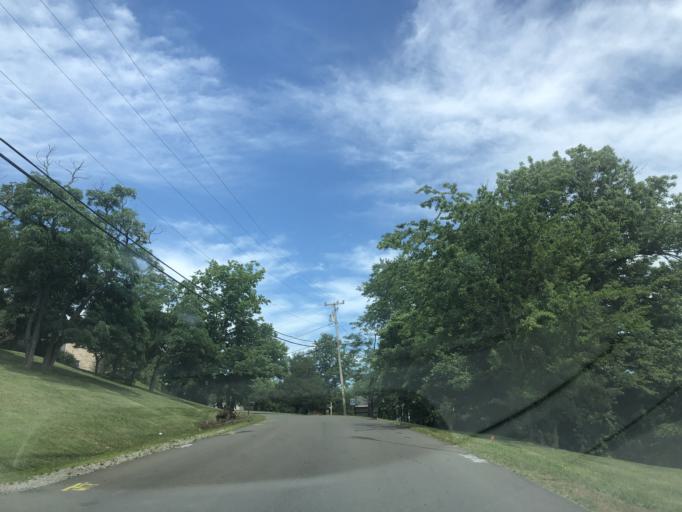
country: US
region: Tennessee
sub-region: Davidson County
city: Belle Meade
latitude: 36.0751
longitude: -86.9342
